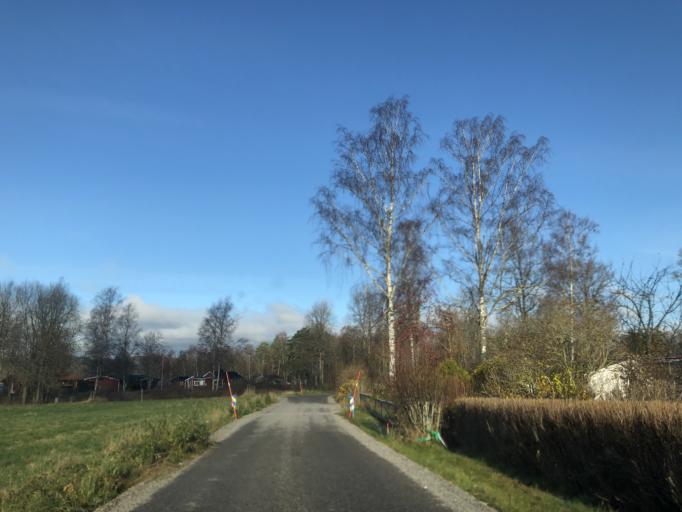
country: SE
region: Vaestra Goetaland
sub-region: Ulricehamns Kommun
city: Ulricehamn
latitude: 57.7230
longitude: 13.3977
